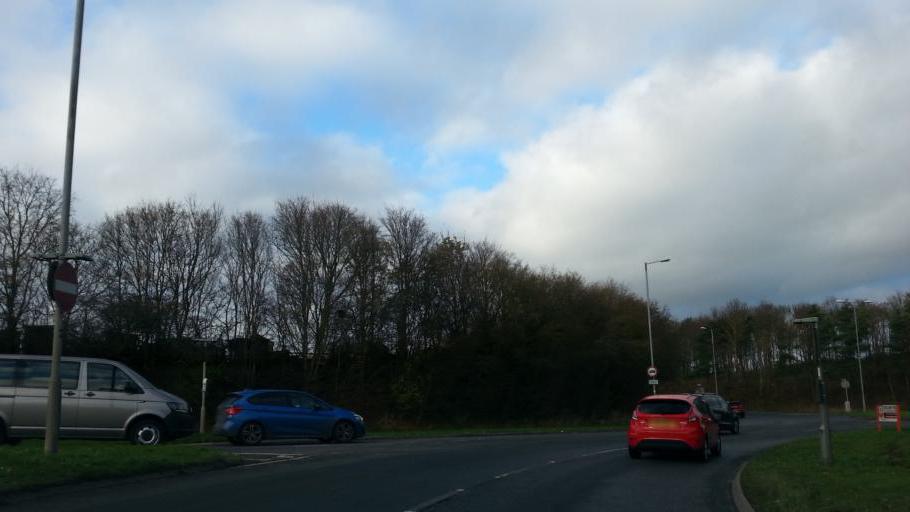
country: GB
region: England
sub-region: Borough of Swindon
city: Wanborough
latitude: 51.5762
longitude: -1.7349
